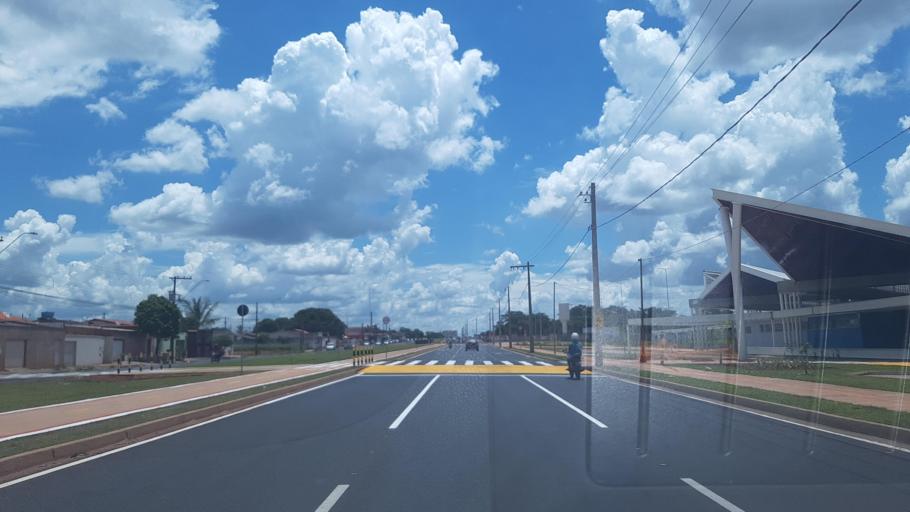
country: BR
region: Minas Gerais
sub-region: Uberlandia
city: Uberlandia
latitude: -18.9529
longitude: -48.3274
